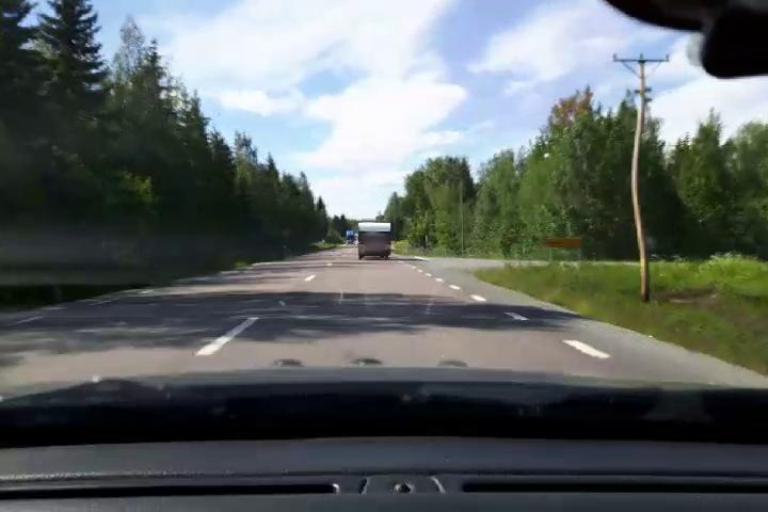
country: SE
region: Gaevleborg
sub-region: Bollnas Kommun
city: Kilafors
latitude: 61.2919
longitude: 16.5009
